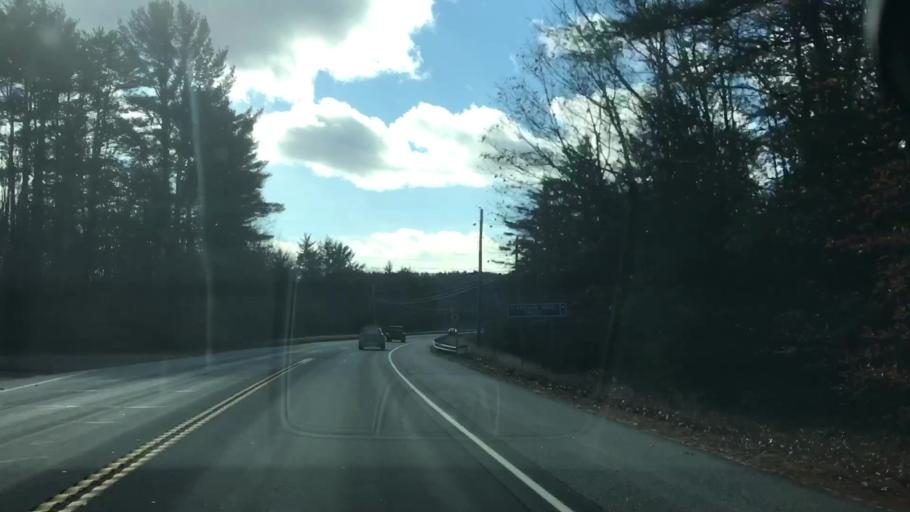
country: US
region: New Hampshire
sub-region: Carroll County
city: Wolfeboro
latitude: 43.5100
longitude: -71.2144
